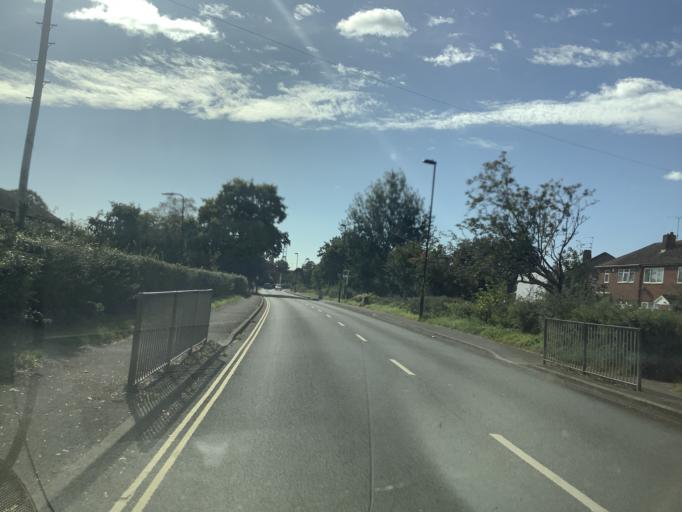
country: GB
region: England
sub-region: Hampshire
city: Marchwood
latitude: 50.9228
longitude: -1.4555
